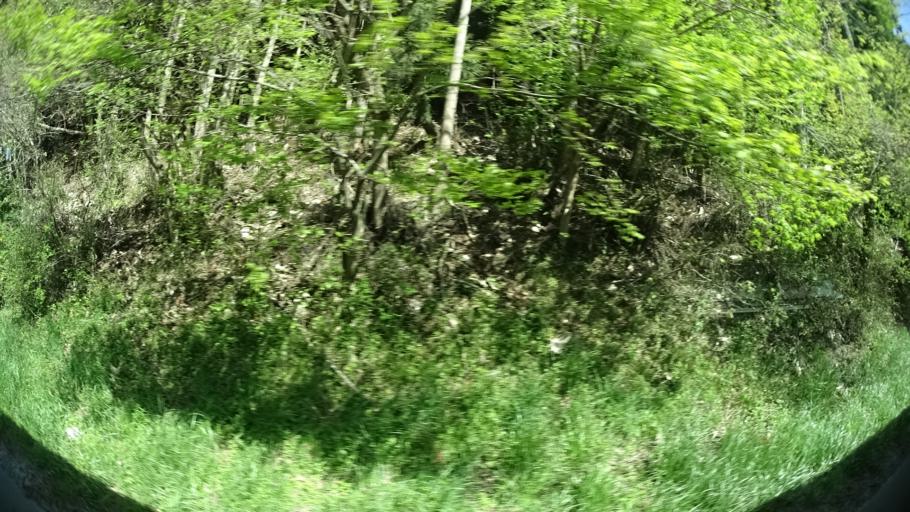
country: JP
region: Iwate
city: Ofunato
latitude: 38.9256
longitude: 141.5955
